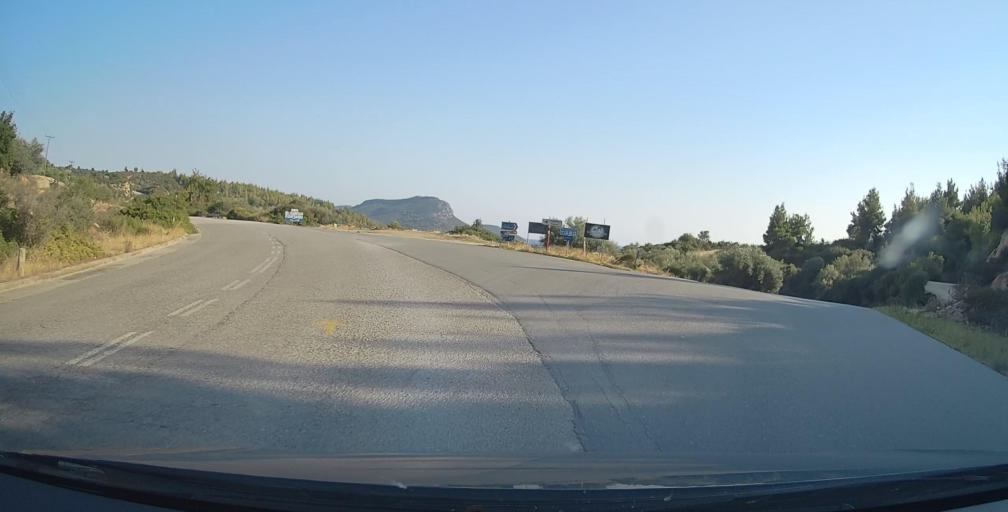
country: GR
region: Central Macedonia
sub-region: Nomos Chalkidikis
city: Sykia
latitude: 39.9993
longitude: 23.8886
